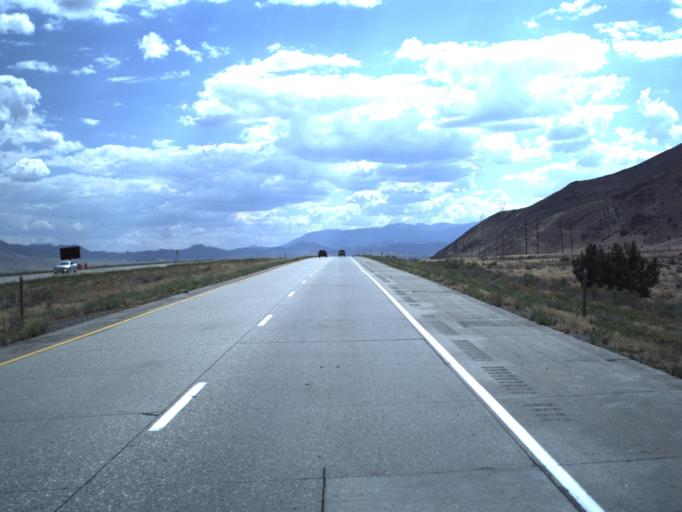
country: US
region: Utah
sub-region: Sevier County
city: Richfield
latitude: 38.7130
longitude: -112.1363
